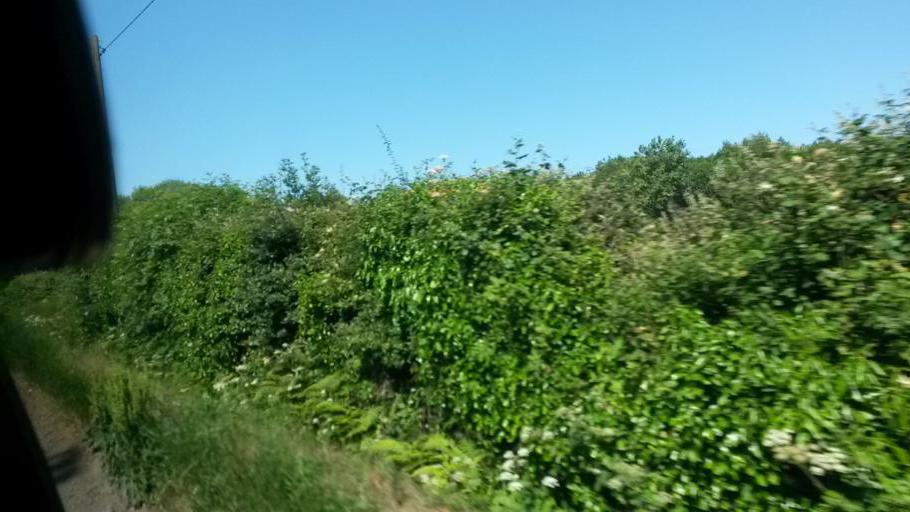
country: IE
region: Leinster
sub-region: An Mhi
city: Stamullin
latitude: 53.5534
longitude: -6.2724
